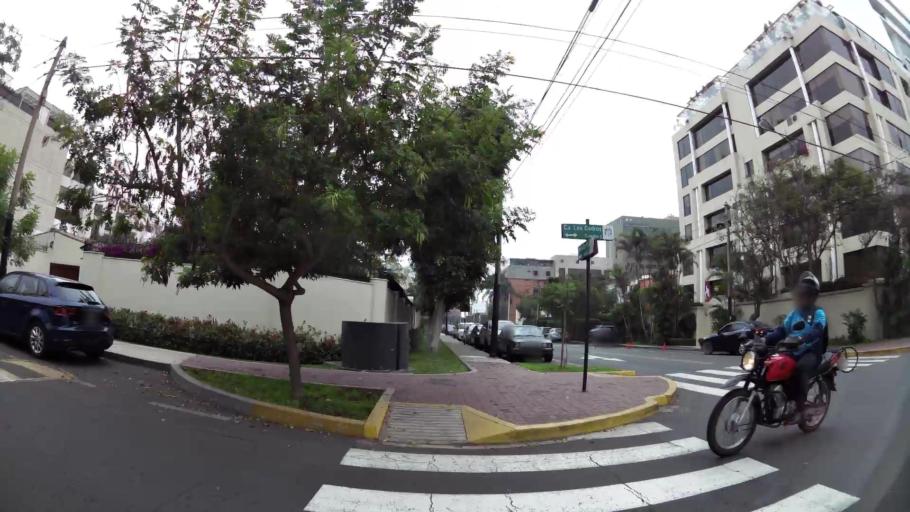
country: PE
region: Lima
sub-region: Lima
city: San Isidro
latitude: -12.0969
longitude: -77.0435
